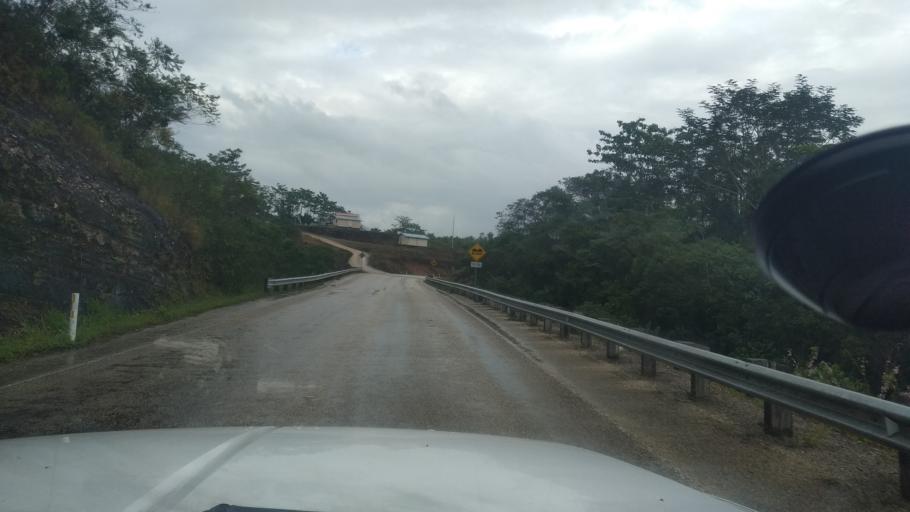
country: GT
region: Peten
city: San Luis
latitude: 16.1876
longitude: -89.1902
